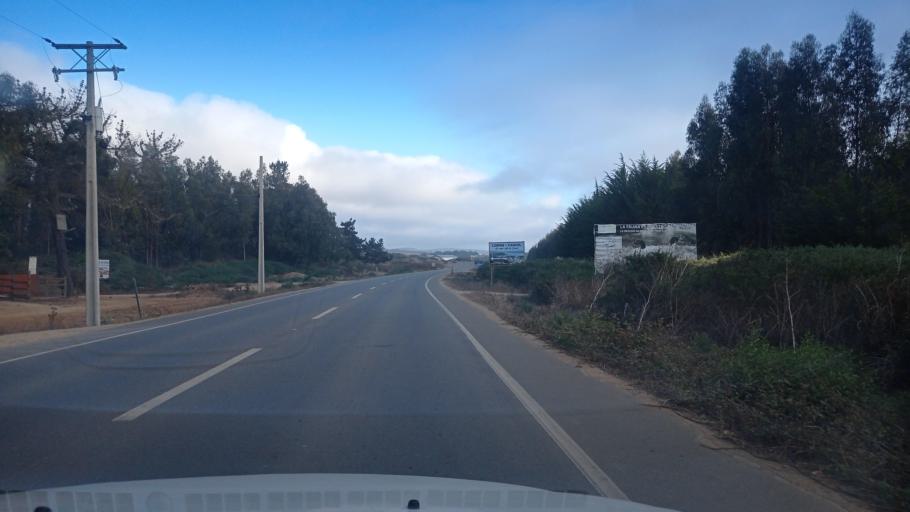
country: CL
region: O'Higgins
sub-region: Provincia de Colchagua
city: Santa Cruz
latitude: -34.4700
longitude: -72.0184
